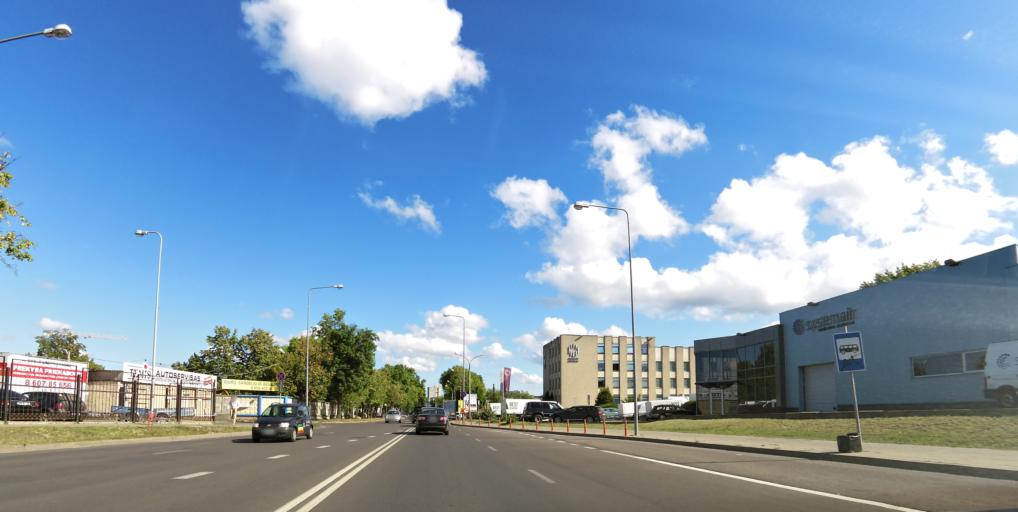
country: LT
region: Vilnius County
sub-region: Vilnius
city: Vilnius
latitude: 54.7129
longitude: 25.2929
